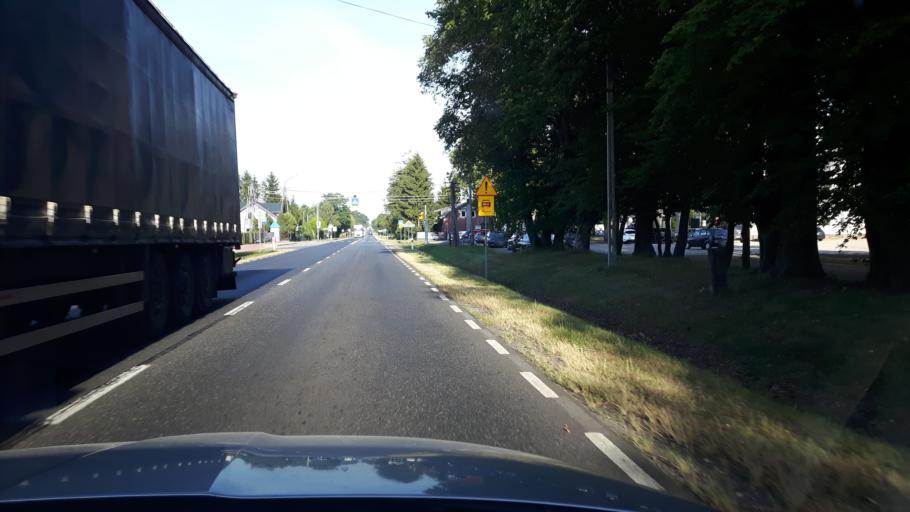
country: PL
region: Masovian Voivodeship
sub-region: Powiat legionowski
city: Wieliszew
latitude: 52.5047
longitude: 20.9887
